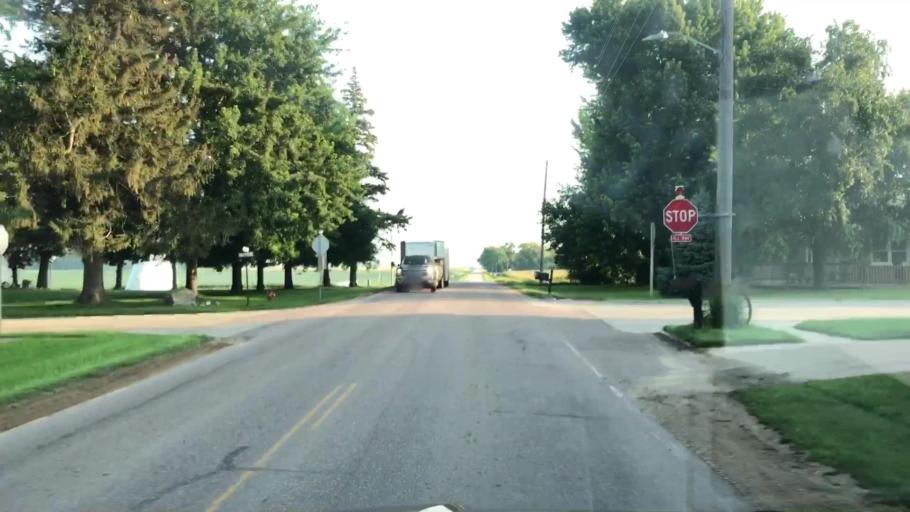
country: US
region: Iowa
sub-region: Sioux County
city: Hull
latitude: 43.1928
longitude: -96.0002
